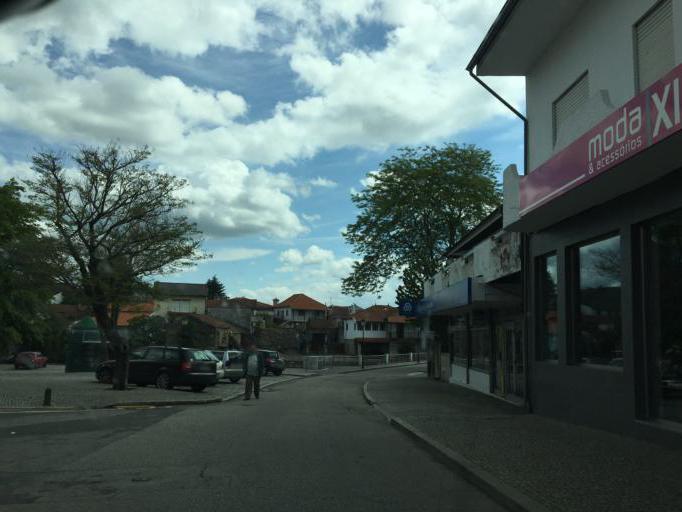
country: PT
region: Vila Real
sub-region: Boticas
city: Boticas
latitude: 41.6880
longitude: -7.6668
